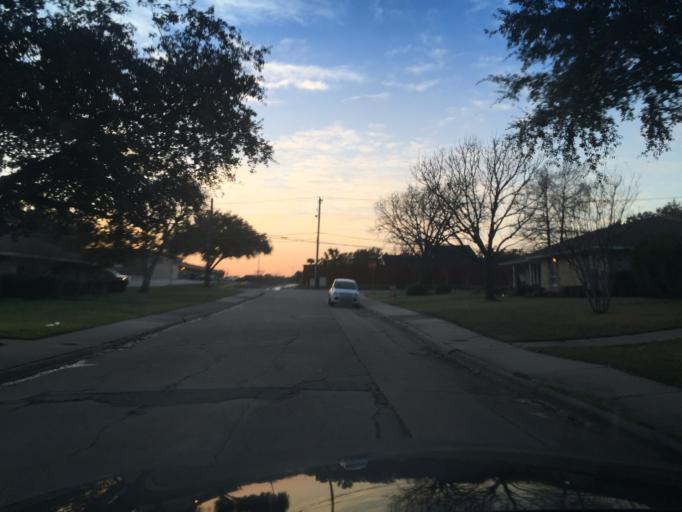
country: US
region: Texas
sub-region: Dallas County
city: Carrollton
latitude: 32.9821
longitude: -96.8966
